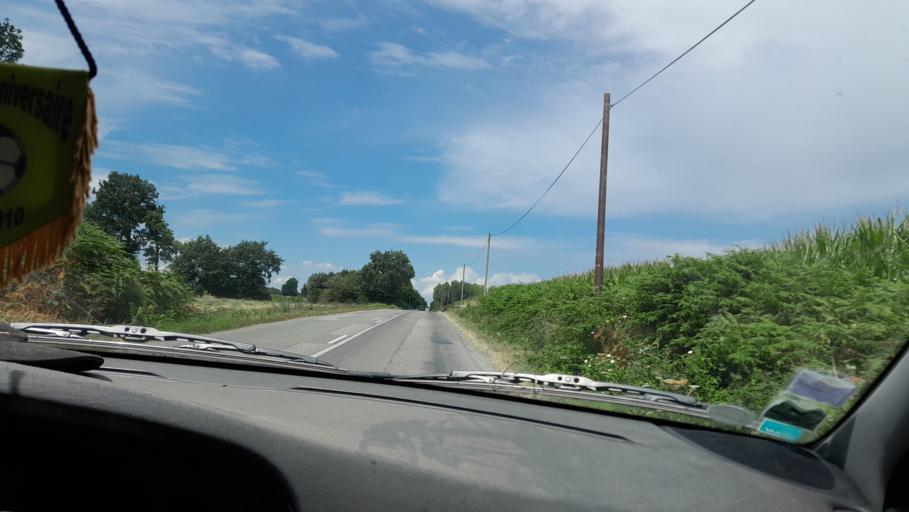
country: FR
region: Brittany
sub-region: Departement d'Ille-et-Vilaine
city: Luitre
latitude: 48.2285
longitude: -1.1007
